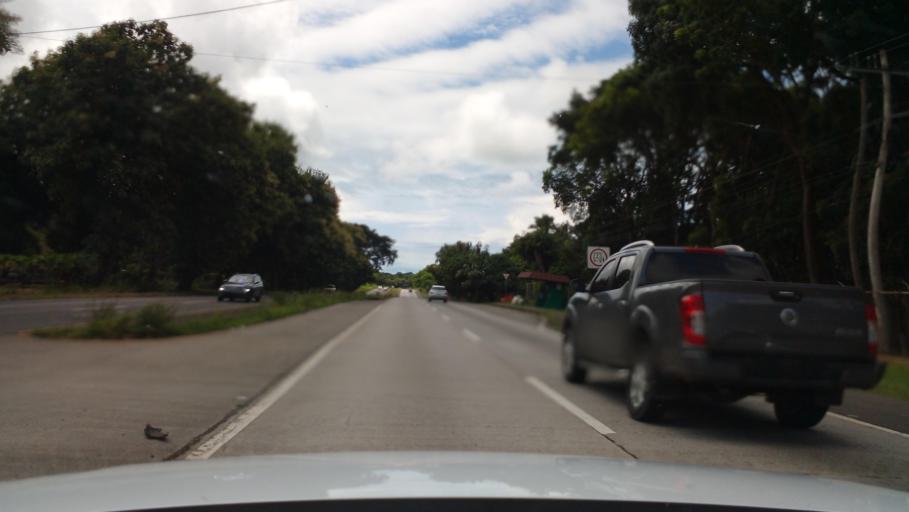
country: PA
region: Cocle
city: Rio Hato
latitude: 8.3846
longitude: -80.1832
